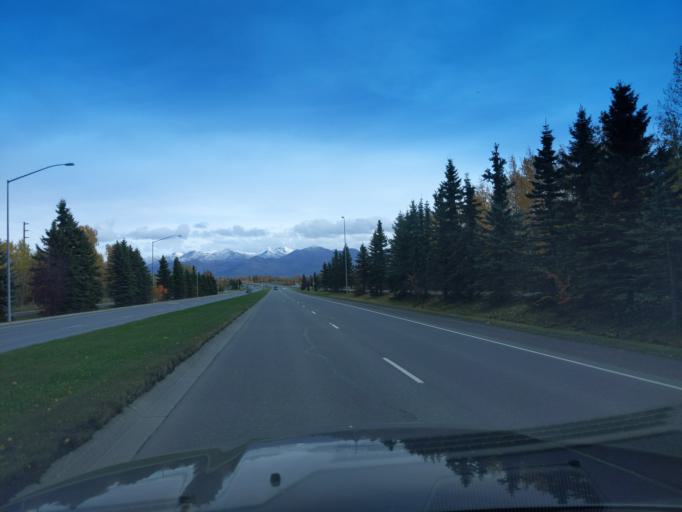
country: US
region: Alaska
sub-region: Anchorage Municipality
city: Anchorage
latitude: 61.1732
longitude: -149.9337
